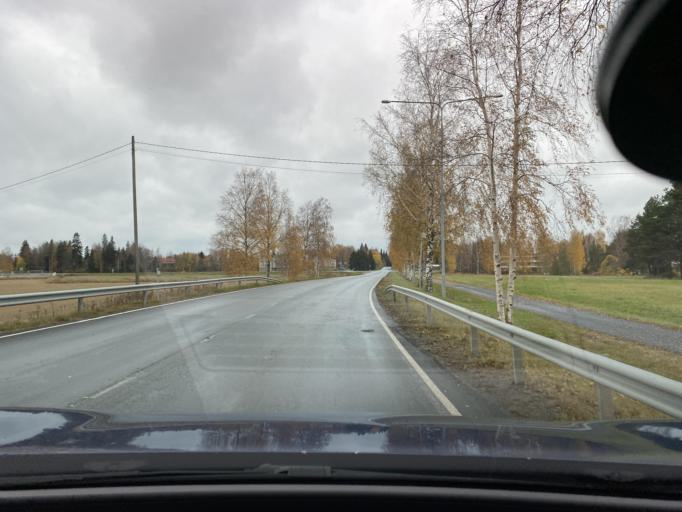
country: FI
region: Satakunta
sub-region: Pori
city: Kokemaeki
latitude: 61.2557
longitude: 22.3664
